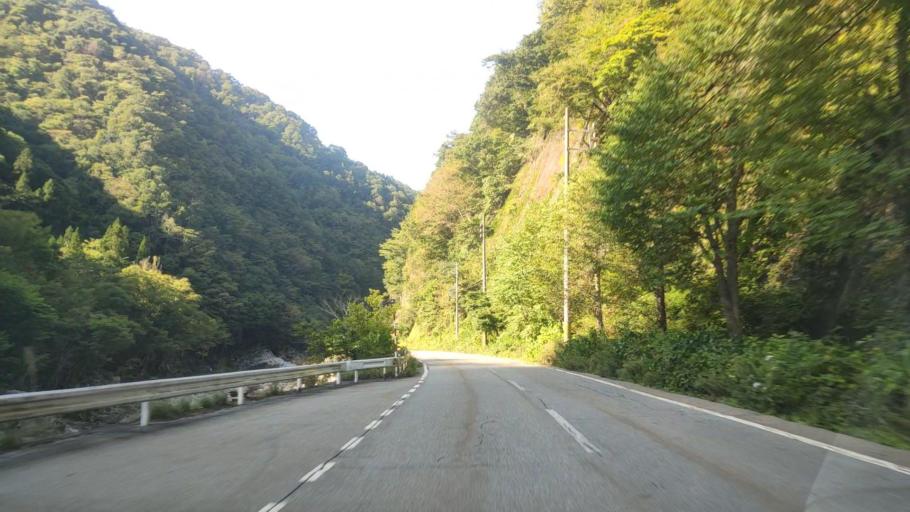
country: JP
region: Gifu
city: Takayama
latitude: 36.2850
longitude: 137.1296
